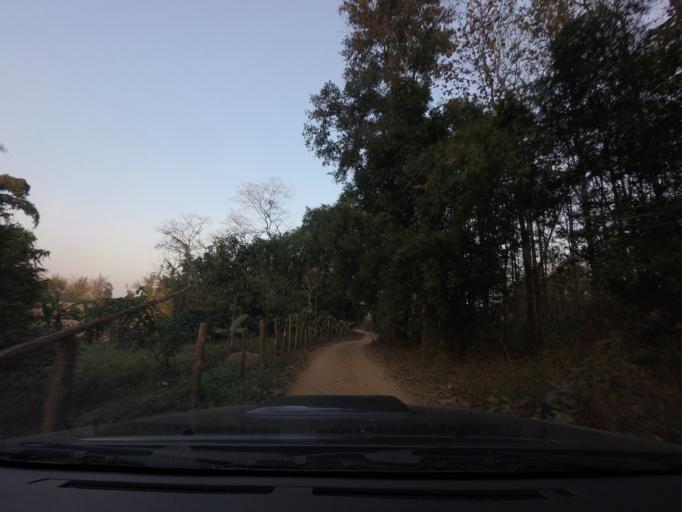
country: TH
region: Chiang Mai
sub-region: Amphoe Chiang Dao
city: Chiang Dao
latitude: 19.3629
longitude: 98.9302
